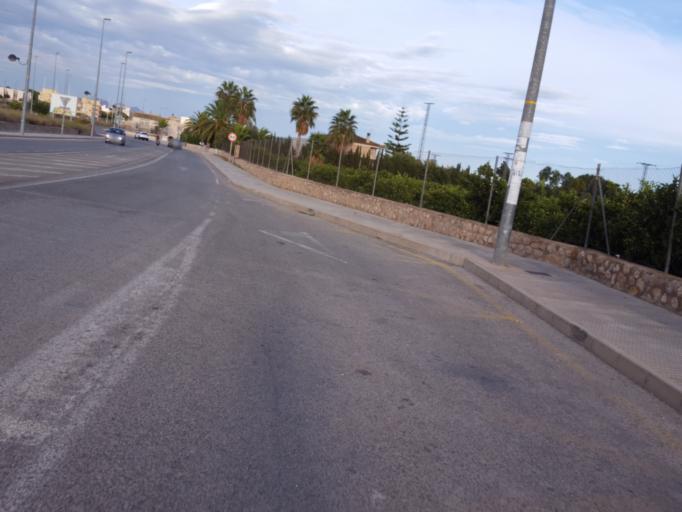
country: ES
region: Murcia
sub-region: Murcia
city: Alcantarilla
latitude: 37.9934
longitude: -1.1810
